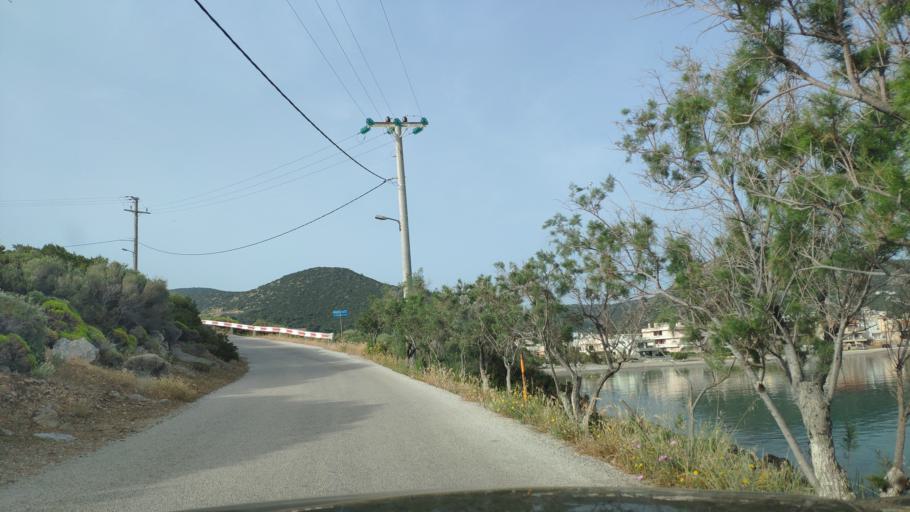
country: GR
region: Attica
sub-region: Nomarchia Anatolikis Attikis
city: Limin Mesoyaias
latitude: 37.8702
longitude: 24.0344
